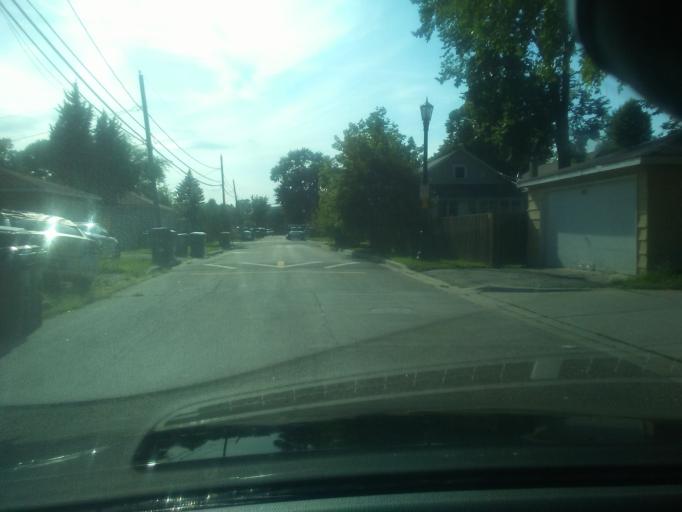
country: US
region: Illinois
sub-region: Cook County
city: Evanston
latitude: 42.0447
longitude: -87.7060
